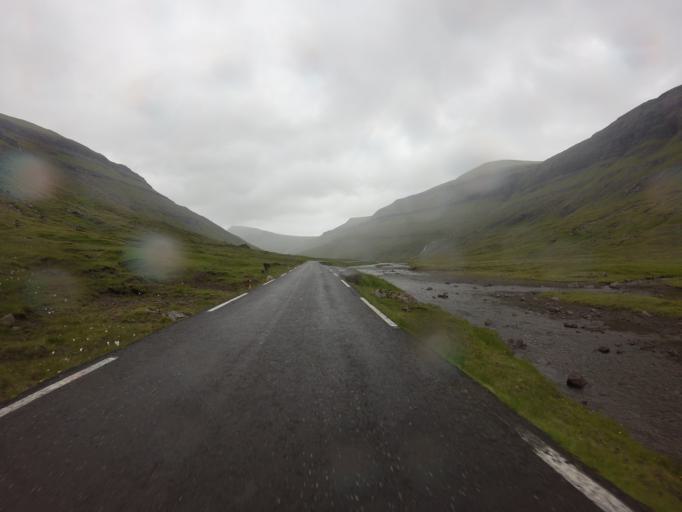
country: FO
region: Streymoy
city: Vestmanna
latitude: 62.2350
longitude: -7.1438
